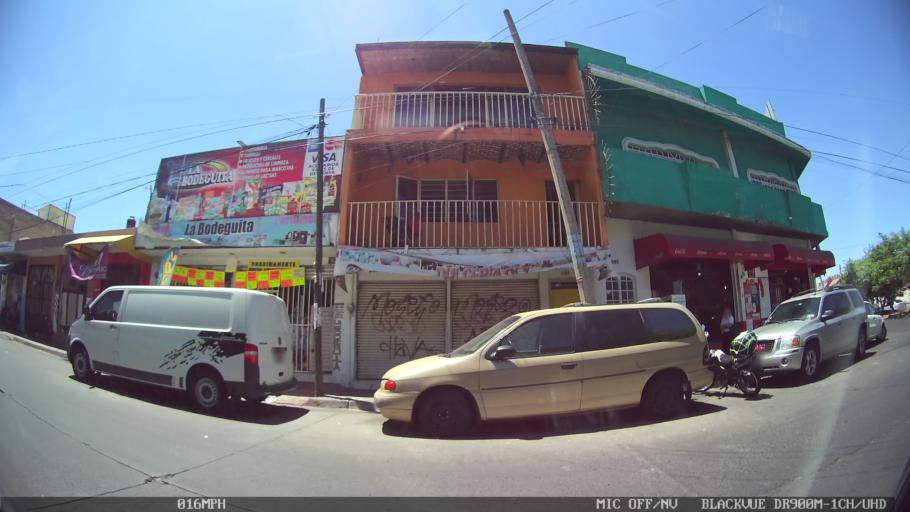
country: MX
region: Jalisco
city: Tlaquepaque
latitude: 20.6856
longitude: -103.2812
